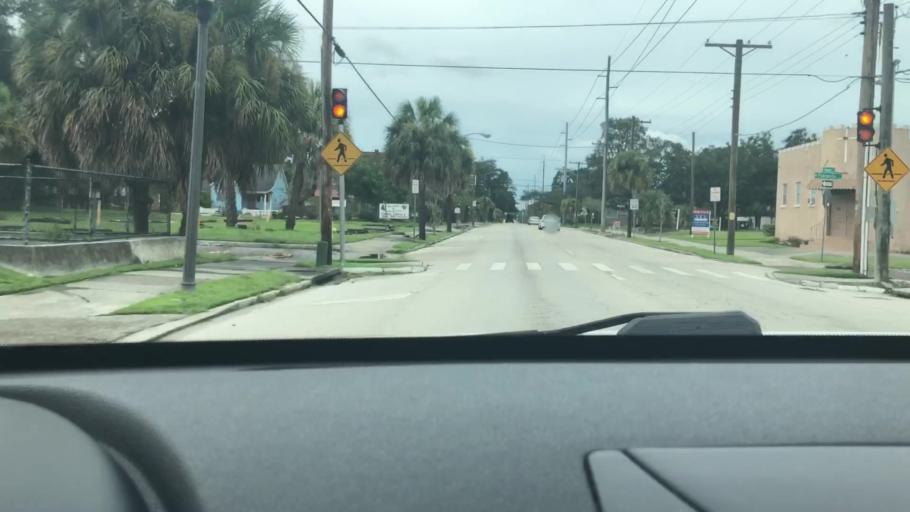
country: US
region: Florida
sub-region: Hillsborough County
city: Tampa
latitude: 27.9621
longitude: -82.4829
